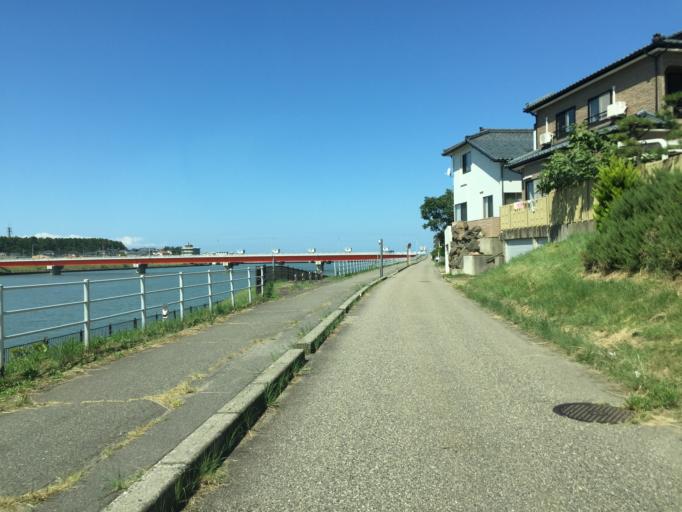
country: JP
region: Niigata
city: Niigata-shi
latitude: 37.9034
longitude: 139.0083
